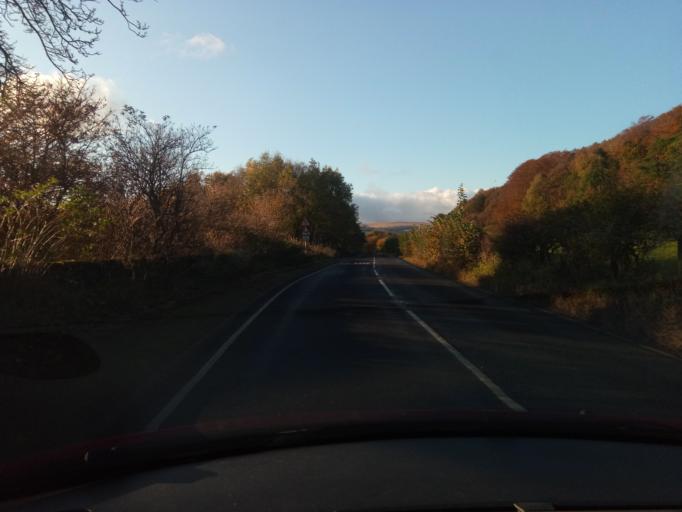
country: GB
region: England
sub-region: County Durham
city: Stanhope
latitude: 54.7342
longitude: -1.9818
